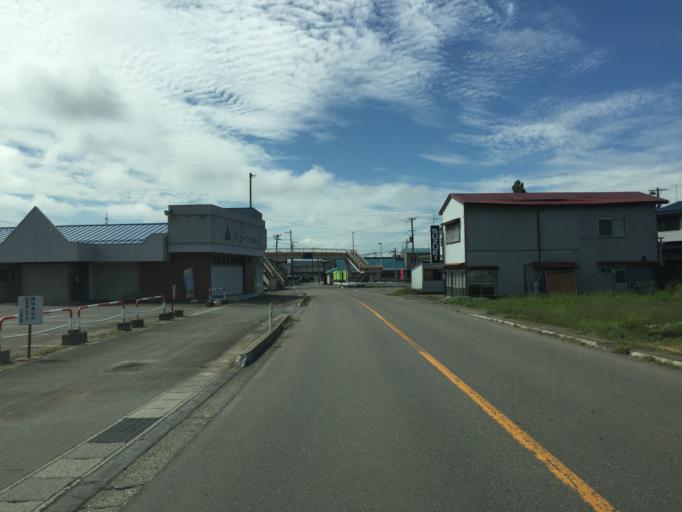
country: JP
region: Fukushima
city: Inawashiro
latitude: 37.5603
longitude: 139.9882
